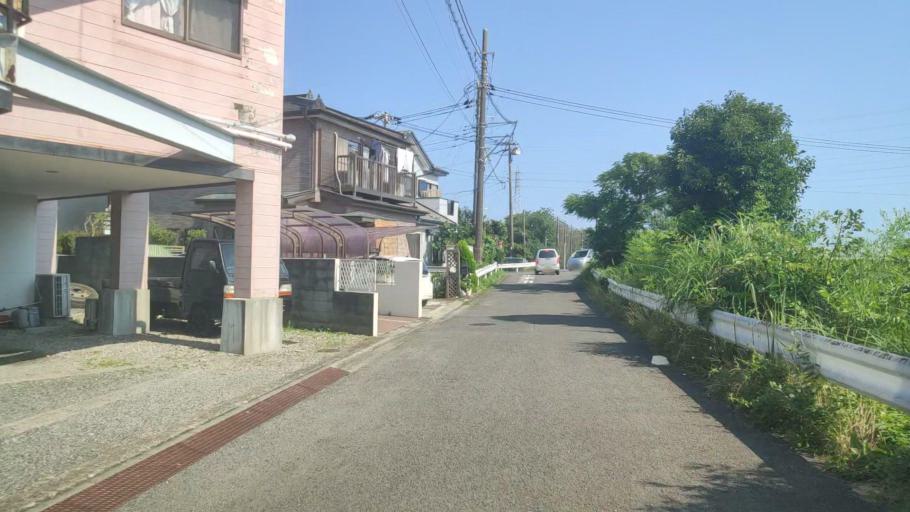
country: JP
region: Kanagawa
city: Hiratsuka
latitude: 35.3514
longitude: 139.3241
